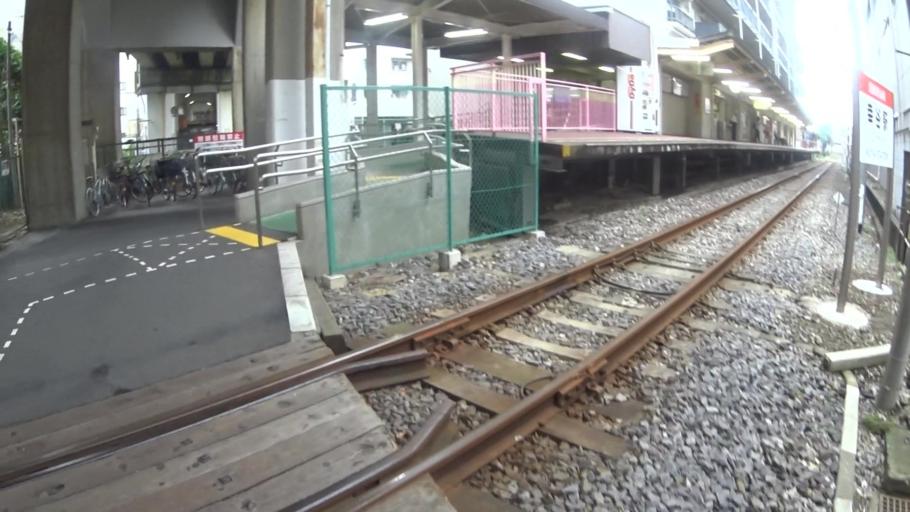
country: JP
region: Chiba
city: Nagareyama
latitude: 35.8261
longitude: 139.9199
